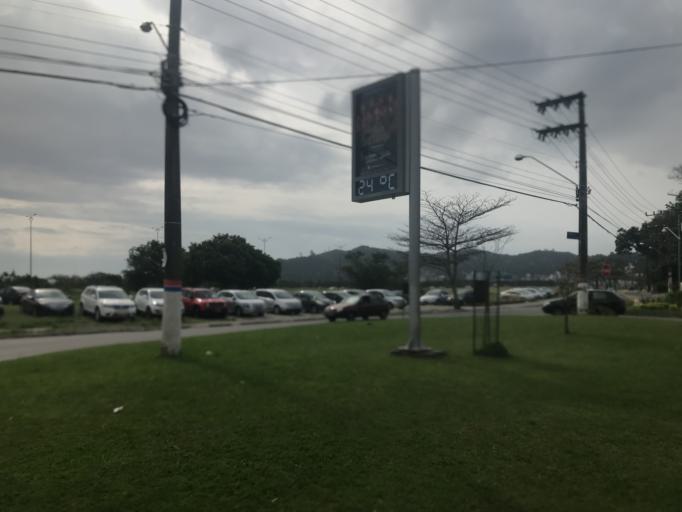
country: BR
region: Santa Catarina
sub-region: Florianopolis
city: Costeira do Pirajubae
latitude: -27.6220
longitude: -48.5264
